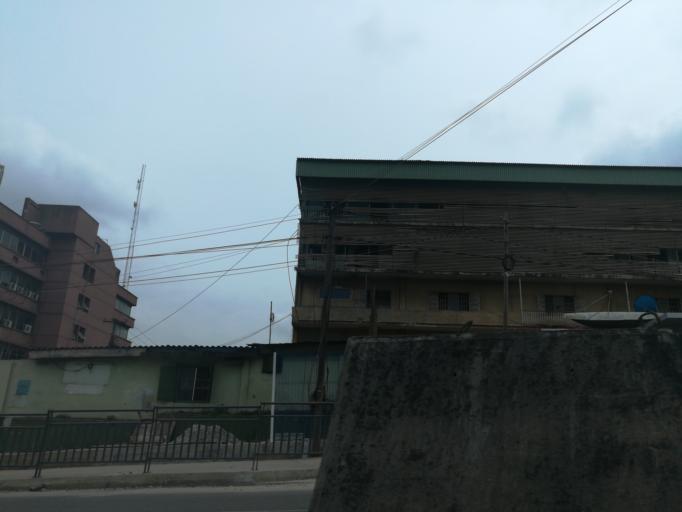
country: NG
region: Lagos
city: Ojota
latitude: 6.5953
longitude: 3.3700
